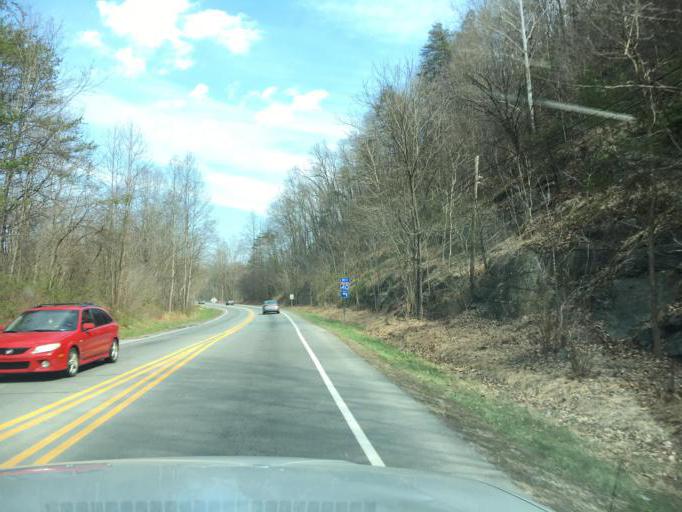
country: US
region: North Carolina
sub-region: McDowell County
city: West Marion
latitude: 35.6442
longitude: -82.0383
